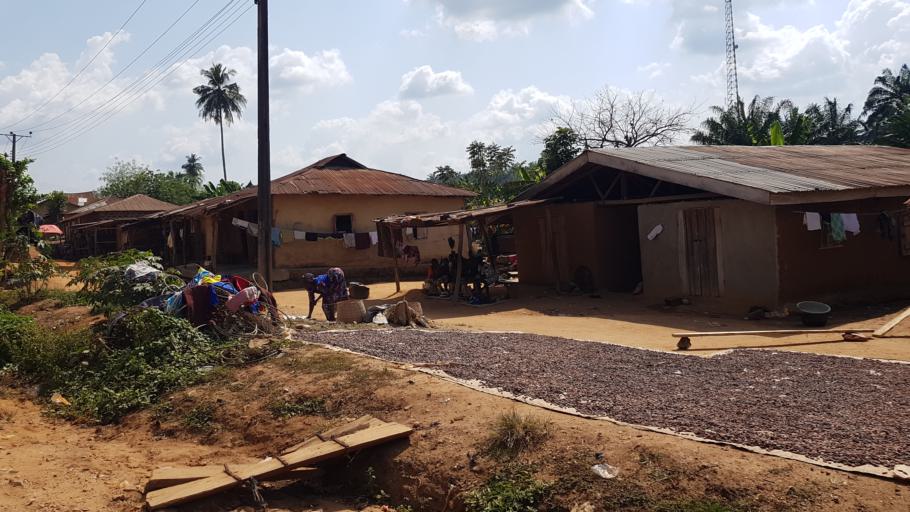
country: NG
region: Osun
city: Ifetedo
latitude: 7.0219
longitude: 4.6311
